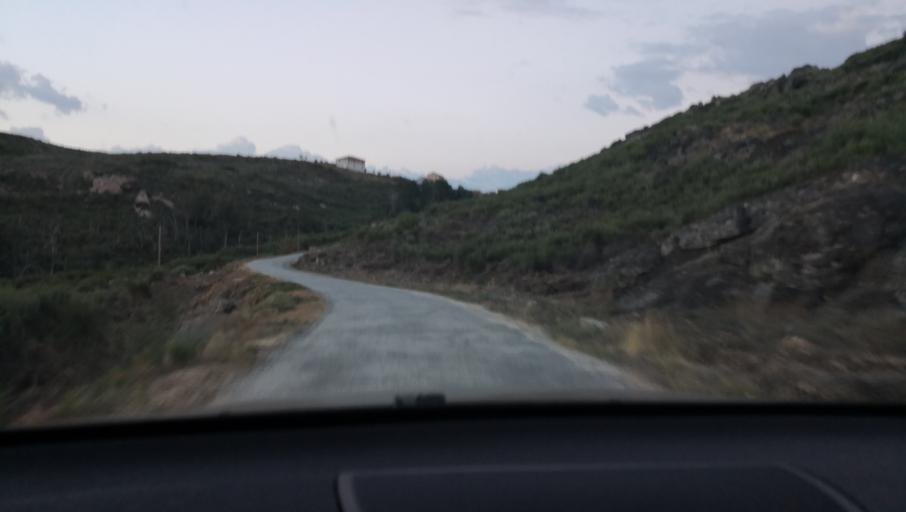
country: PT
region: Vila Real
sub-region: Sabrosa
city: Sabrosa
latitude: 41.2873
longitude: -7.6216
